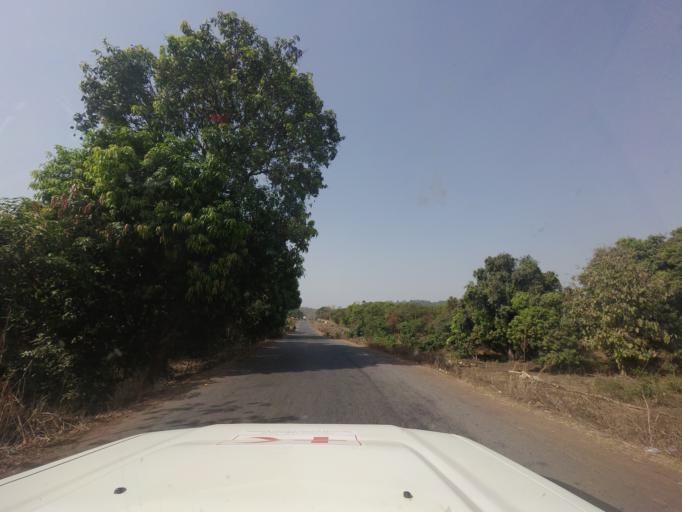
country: GN
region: Mamou
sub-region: Mamou Prefecture
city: Mamou
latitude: 10.1847
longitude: -12.4598
